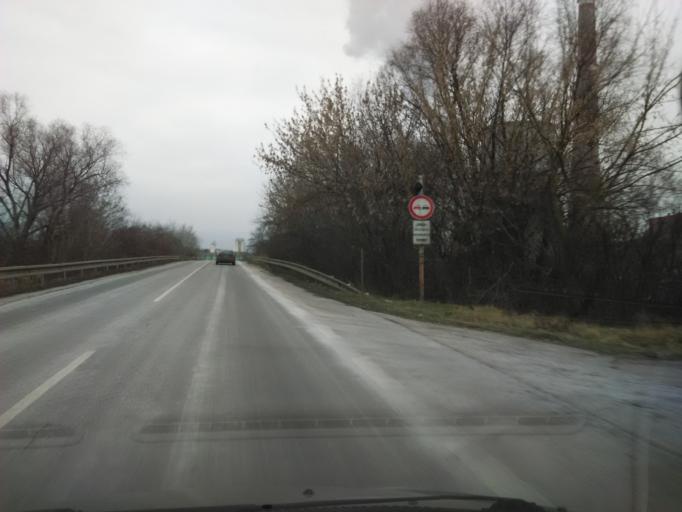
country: SK
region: Nitriansky
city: Novaky
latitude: 48.7025
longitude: 18.5363
